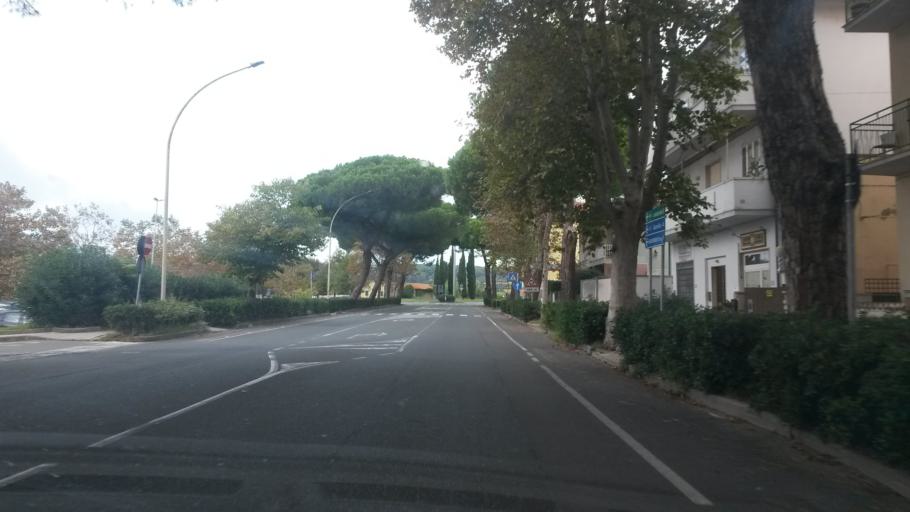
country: IT
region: Tuscany
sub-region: Provincia di Livorno
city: Rosignano Solvay-Castiglioncello
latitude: 43.3962
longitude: 10.4362
